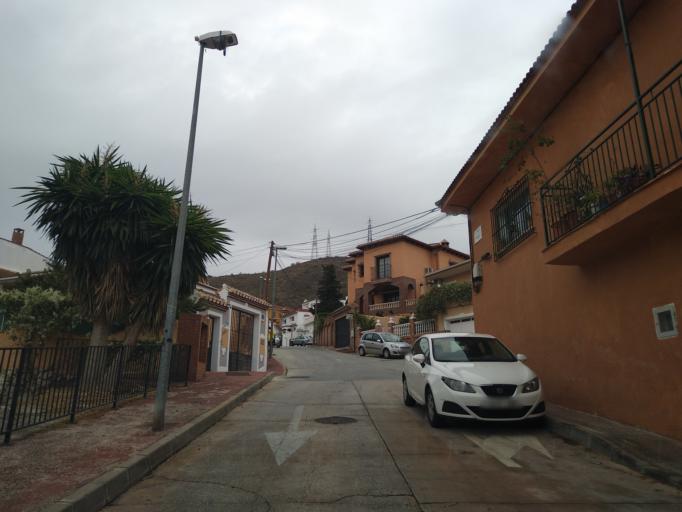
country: ES
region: Andalusia
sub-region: Provincia de Malaga
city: Malaga
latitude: 36.7470
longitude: -4.4770
